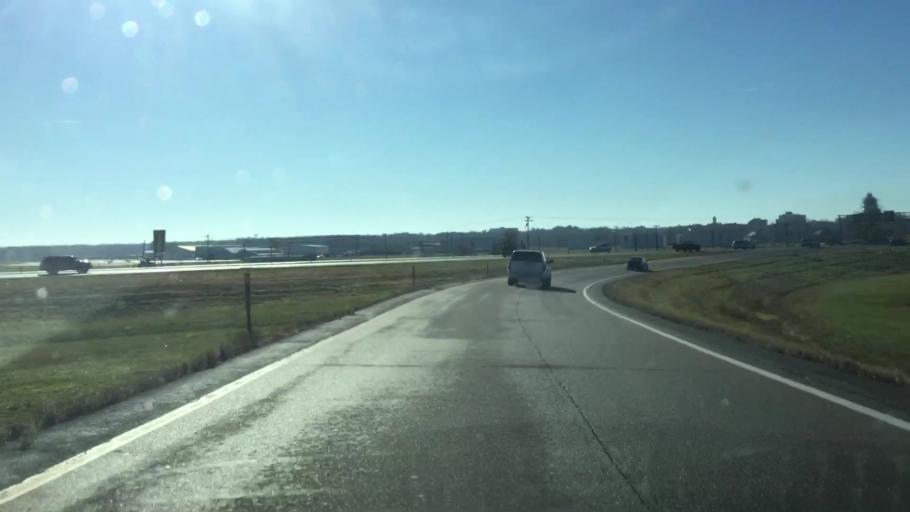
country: US
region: Missouri
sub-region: Cole County
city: Jefferson City
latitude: 38.5990
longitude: -92.1694
